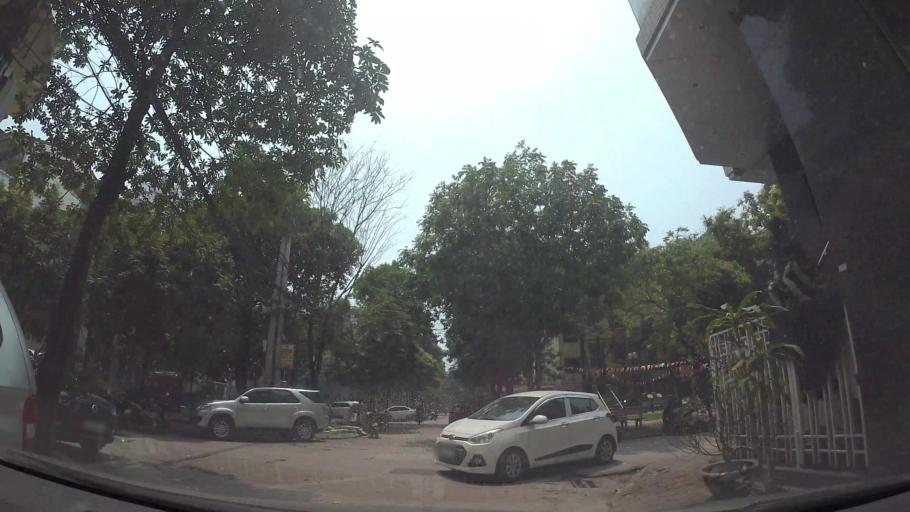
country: VN
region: Ha Noi
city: Thanh Xuan
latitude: 20.9981
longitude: 105.8002
